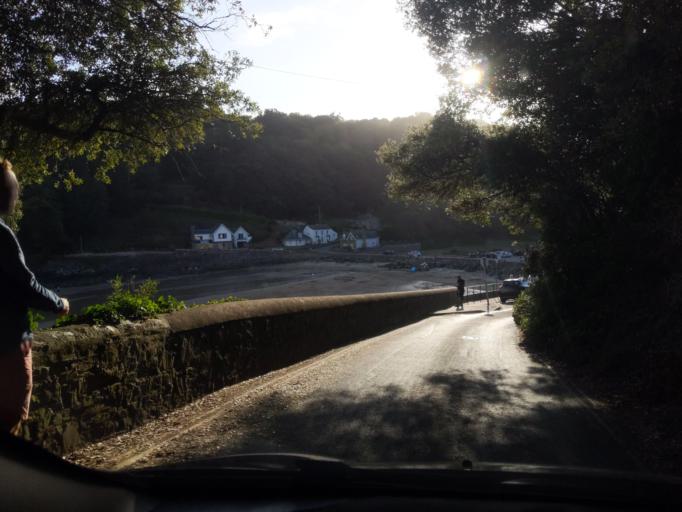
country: GB
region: England
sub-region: Devon
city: Salcombe
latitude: 50.2301
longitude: -3.7793
